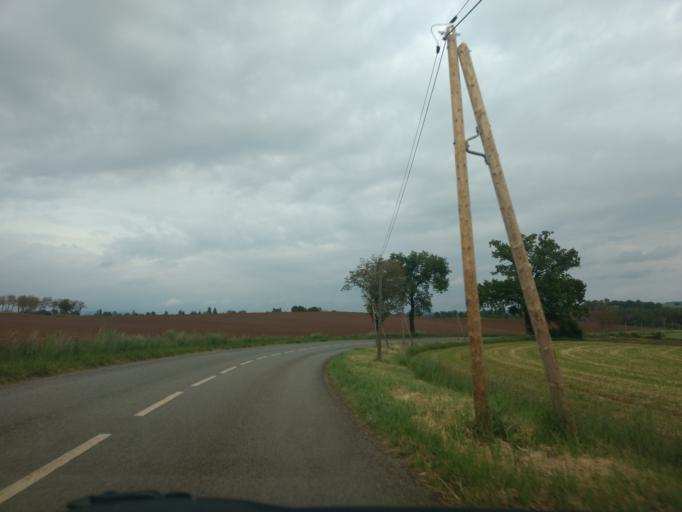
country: FR
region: Midi-Pyrenees
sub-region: Departement de l'Aveyron
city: Montbazens
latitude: 44.4935
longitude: 2.2096
